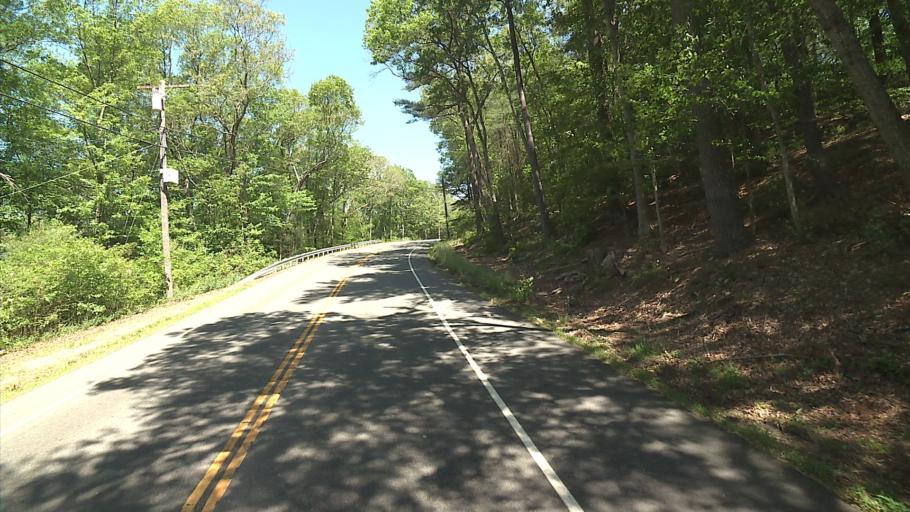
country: US
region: Rhode Island
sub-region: Washington County
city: Hopkinton
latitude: 41.5345
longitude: -71.8385
